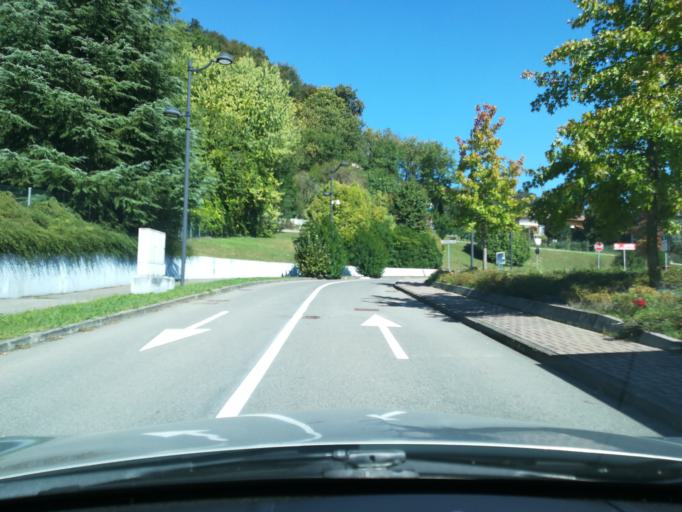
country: IT
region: Lombardy
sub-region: Provincia di Bergamo
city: San Paolo d'Argon
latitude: 45.6849
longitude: 9.7863
